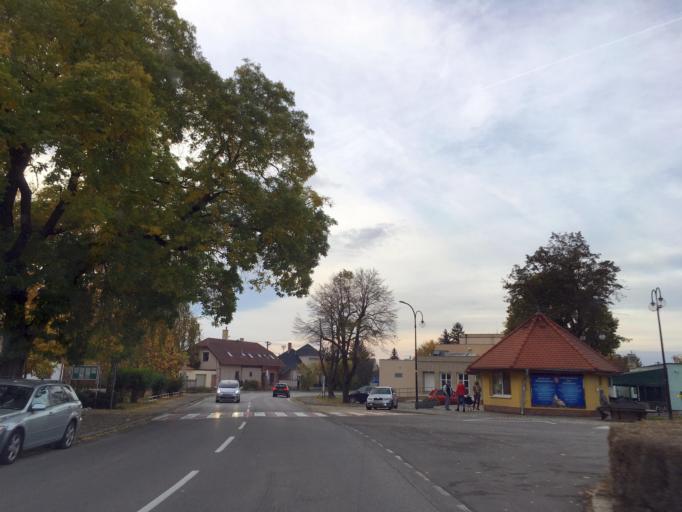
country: SK
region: Trnavsky
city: Samorin
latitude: 48.0991
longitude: 17.3542
